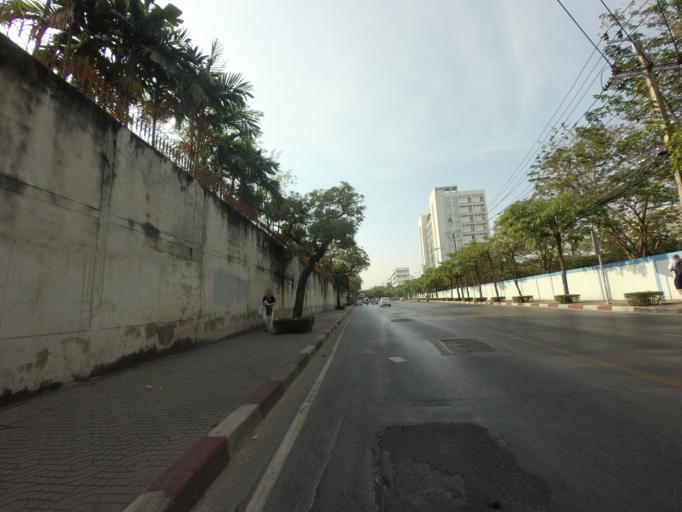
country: TH
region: Bangkok
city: Wang Thonglang
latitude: 13.7531
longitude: 100.6161
